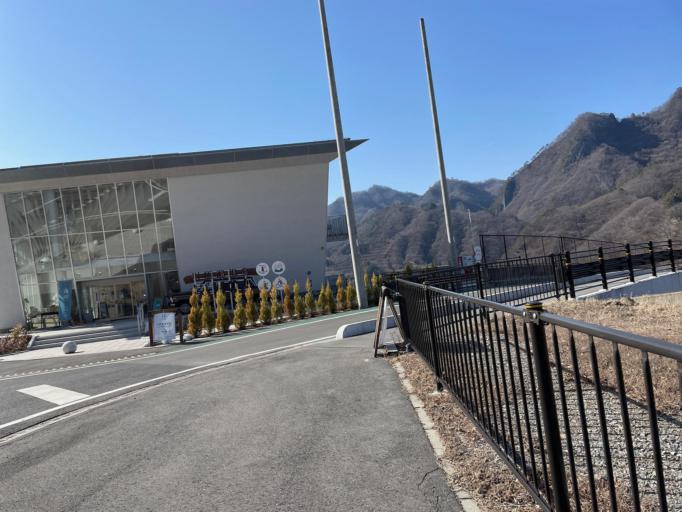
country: JP
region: Gunma
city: Nakanojomachi
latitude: 36.5446
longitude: 138.6966
